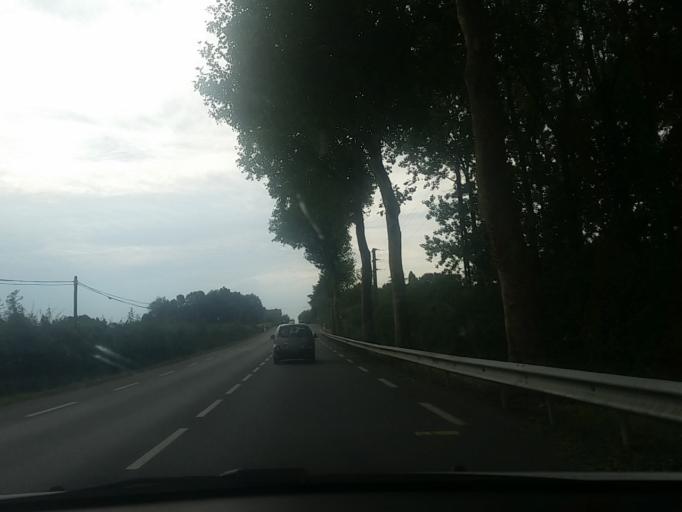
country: FR
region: Pays de la Loire
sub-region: Departement de la Vendee
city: Saint-Fulgent
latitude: 46.8756
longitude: -1.2033
